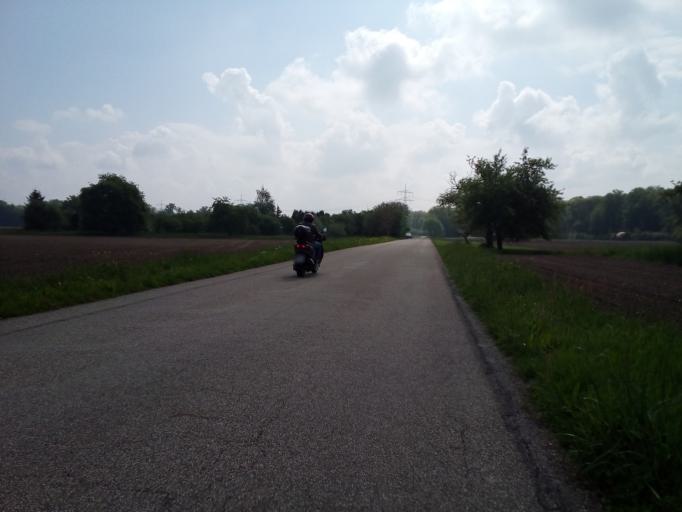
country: DE
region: Baden-Wuerttemberg
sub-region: Freiburg Region
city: Rheinau
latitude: 48.6601
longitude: 7.9489
